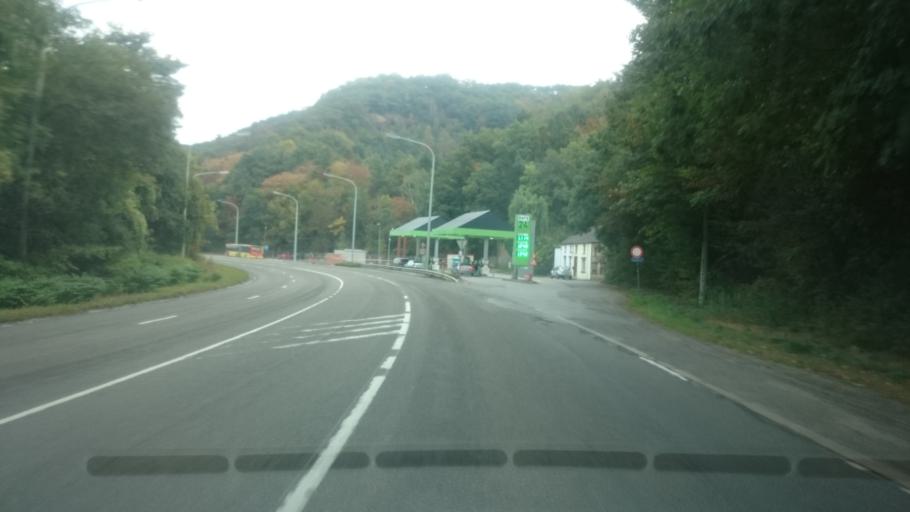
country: BE
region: Wallonia
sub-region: Province de Namur
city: Namur
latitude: 50.4497
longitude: 4.8339
